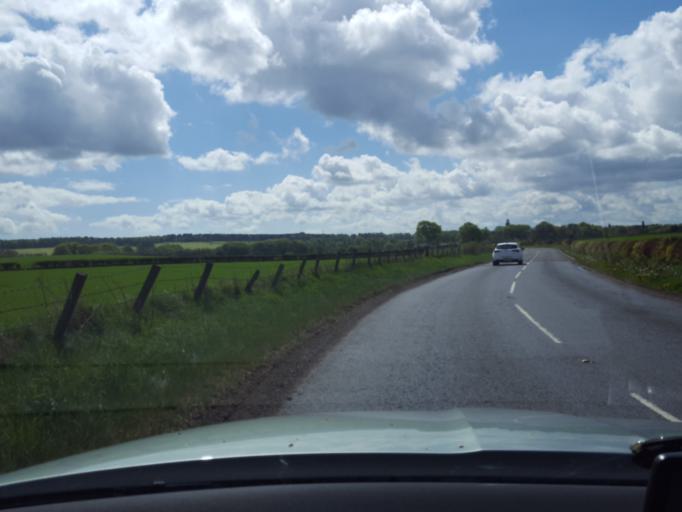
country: GB
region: Scotland
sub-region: Angus
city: Brechin
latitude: 56.7775
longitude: -2.6442
